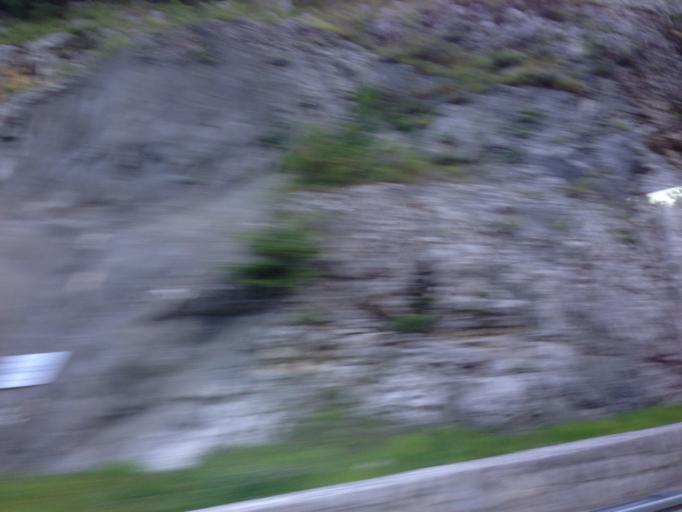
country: HR
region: Primorsko-Goranska
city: Skrljevo
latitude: 45.3198
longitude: 14.4984
